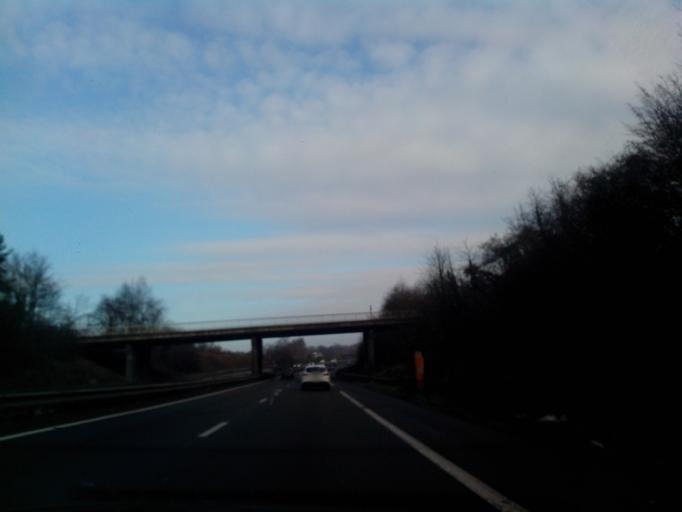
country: FR
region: Ile-de-France
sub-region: Departement du Val-d'Oise
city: Meriel
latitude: 49.0694
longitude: 2.2201
